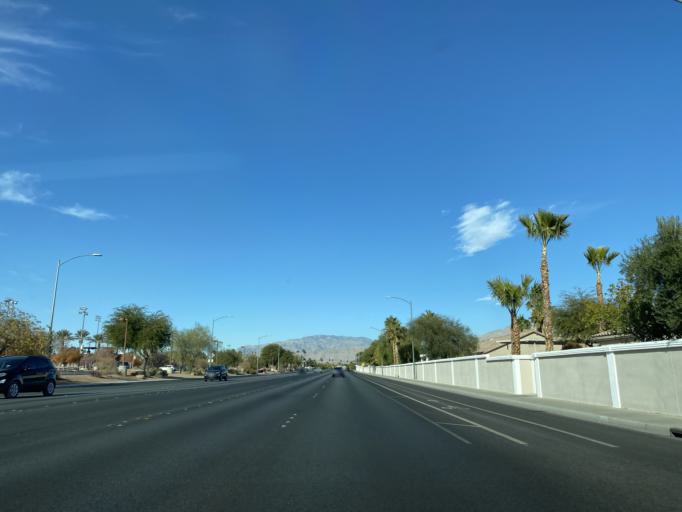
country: US
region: Nevada
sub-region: Clark County
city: Las Vegas
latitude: 36.2873
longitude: -115.2603
